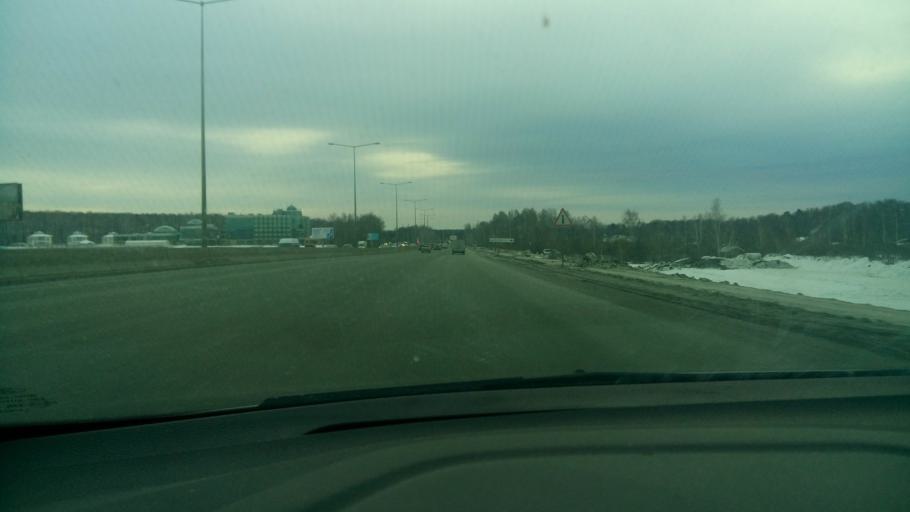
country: RU
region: Sverdlovsk
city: Istok
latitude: 56.7784
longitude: 60.7096
